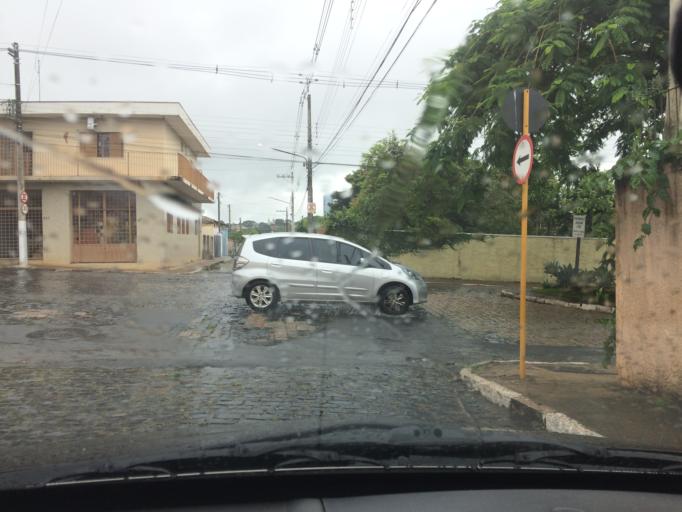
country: BR
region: Sao Paulo
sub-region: Casa Branca
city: Casa Branca
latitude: -21.7722
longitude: -47.0891
